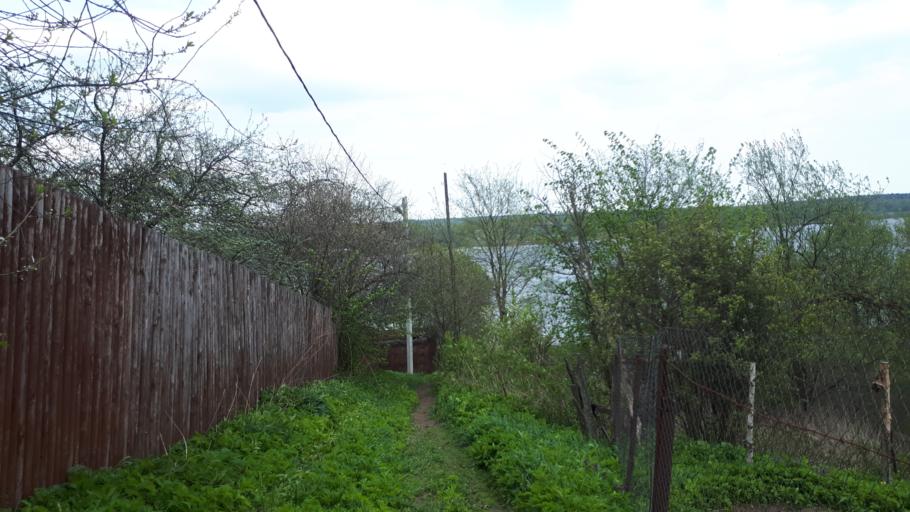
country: RU
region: Jaroslavl
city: Konstantinovskiy
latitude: 57.8339
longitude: 39.5945
